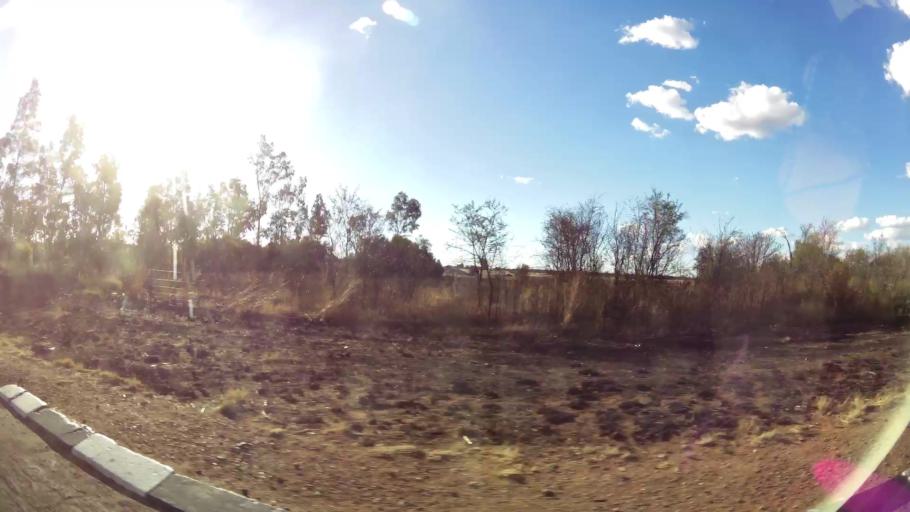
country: ZA
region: North-West
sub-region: Dr Kenneth Kaunda District Municipality
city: Stilfontein
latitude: -26.8408
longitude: 26.7557
